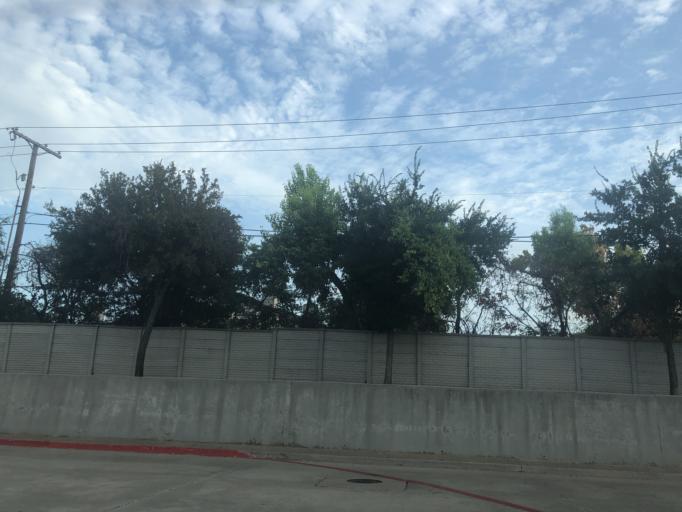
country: US
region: Texas
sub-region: Dallas County
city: Sunnyvale
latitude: 32.8434
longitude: -96.5973
